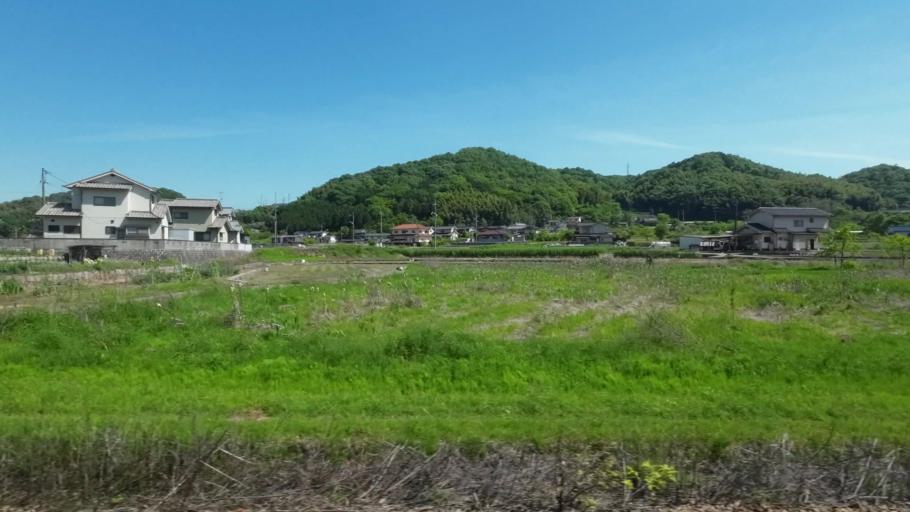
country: JP
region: Hiroshima
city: Fukuyama
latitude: 34.4654
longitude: 133.2937
